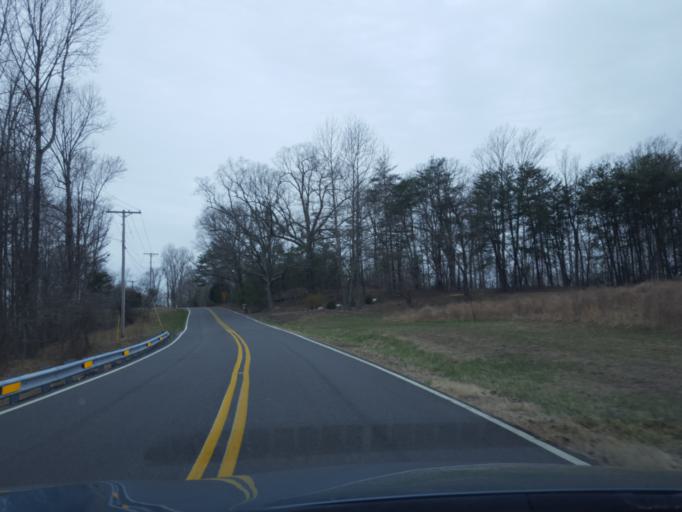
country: US
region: Maryland
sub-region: Calvert County
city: Prince Frederick
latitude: 38.4886
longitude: -76.5721
